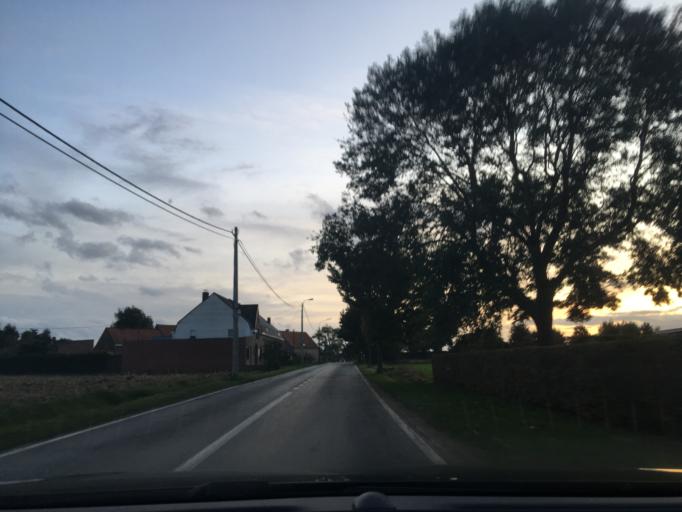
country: BE
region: Flanders
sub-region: Provincie West-Vlaanderen
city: Moorslede
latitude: 50.9277
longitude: 3.0509
